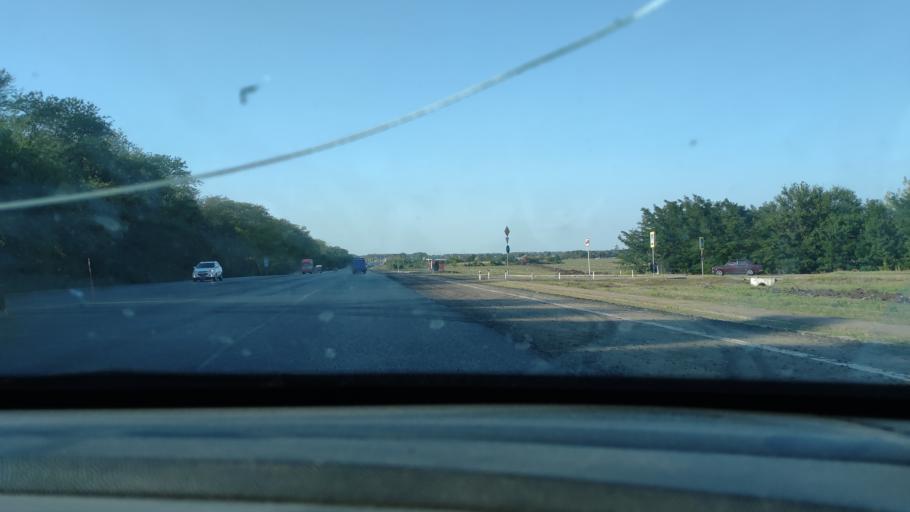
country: RU
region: Krasnodarskiy
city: Medvedovskaya
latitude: 45.5054
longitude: 38.9420
